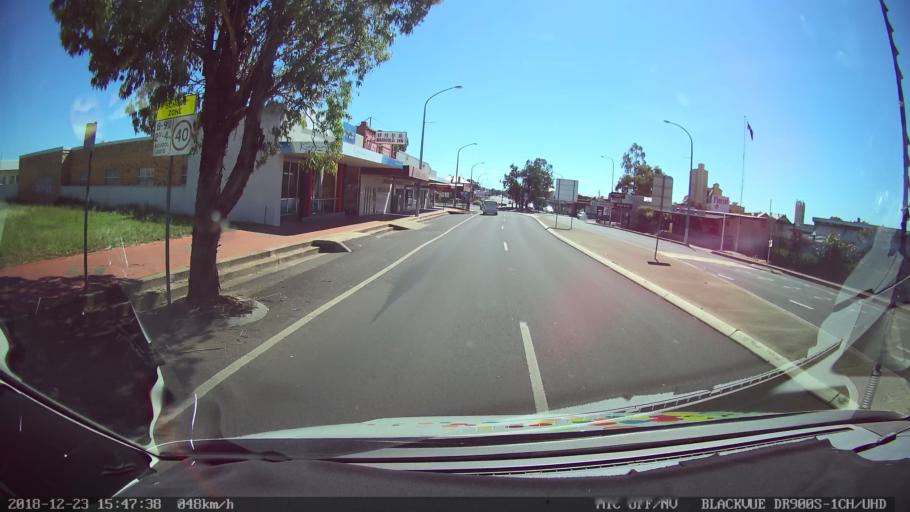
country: AU
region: New South Wales
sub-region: Tamworth Municipality
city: Tamworth
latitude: -31.0933
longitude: 150.9188
